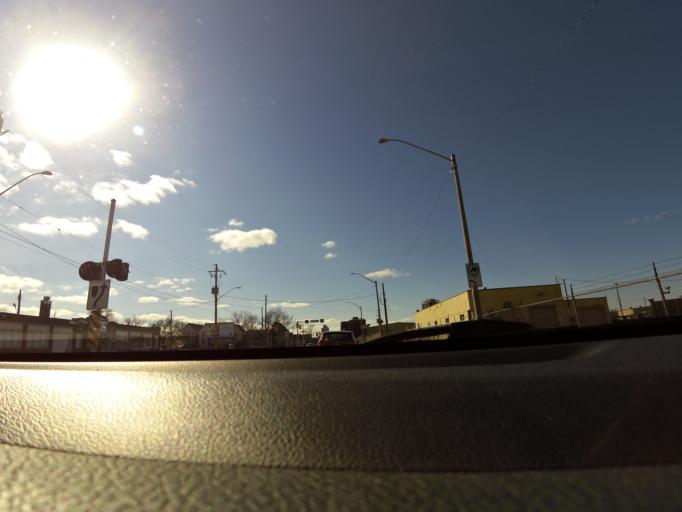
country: CA
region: Ontario
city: Hamilton
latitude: 43.2699
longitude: -79.8510
